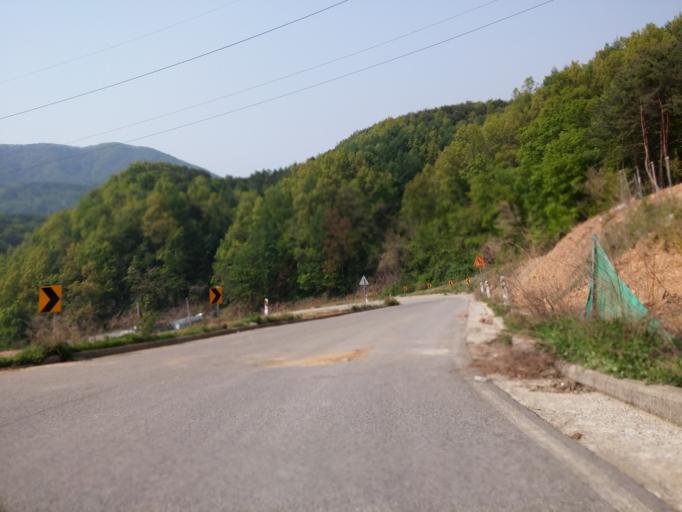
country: KR
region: Chungcheongbuk-do
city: Okcheon
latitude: 36.3889
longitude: 127.6036
